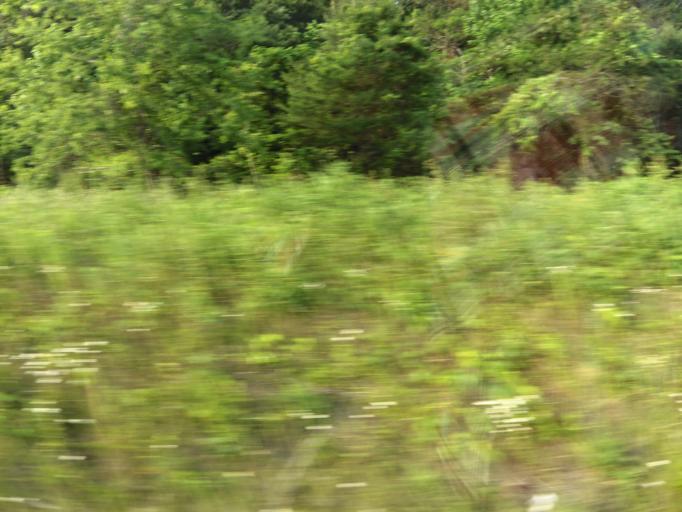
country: US
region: Tennessee
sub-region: Sevier County
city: Sevierville
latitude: 35.8320
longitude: -83.6151
